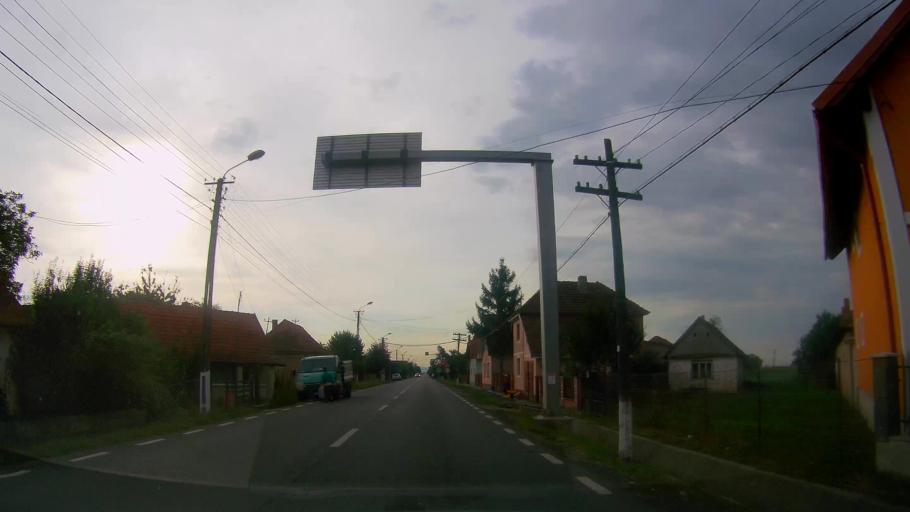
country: RO
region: Satu Mare
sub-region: Comuna Halmeu
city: Halmeu
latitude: 47.9742
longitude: 23.0294
